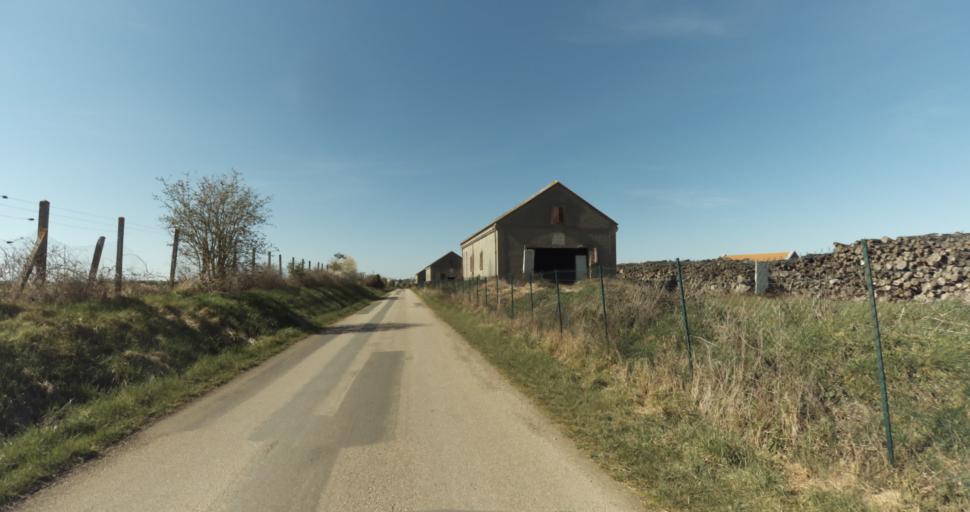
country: FR
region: Lower Normandy
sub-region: Departement du Calvados
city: Saint-Pierre-sur-Dives
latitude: 49.0472
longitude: -0.0486
